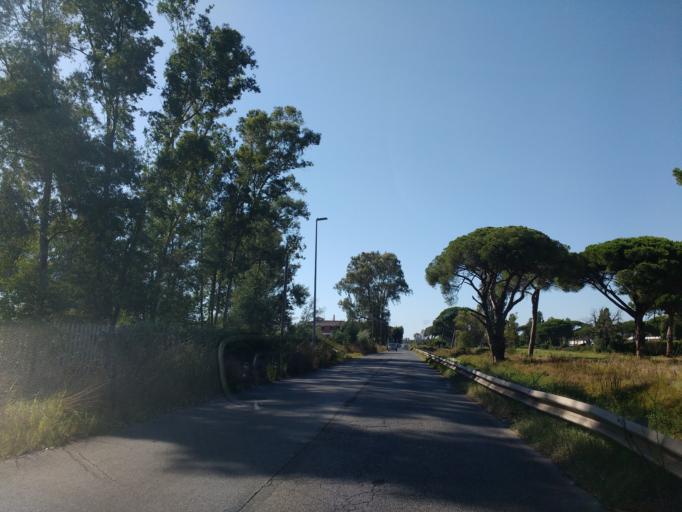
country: IT
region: Latium
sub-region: Citta metropolitana di Roma Capitale
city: Acilia-Castel Fusano-Ostia Antica
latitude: 41.7389
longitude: 12.3430
